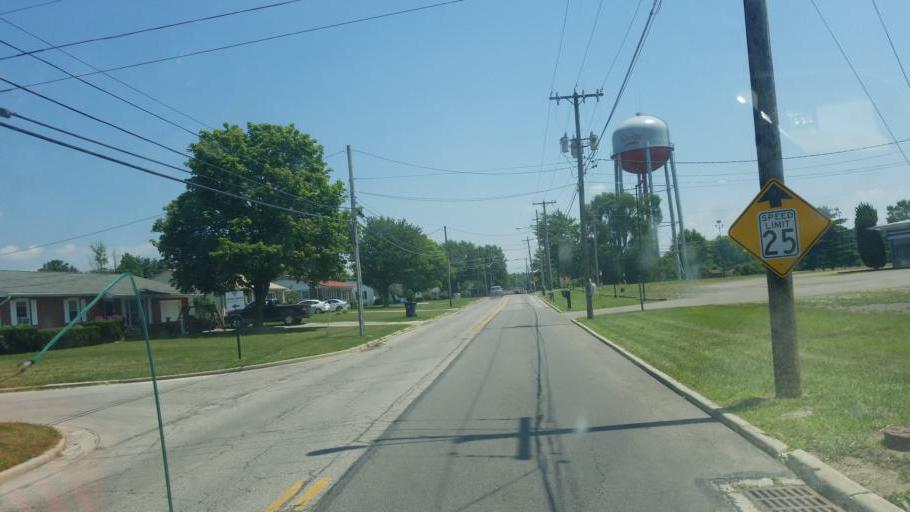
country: US
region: Ohio
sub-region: Richland County
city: Shelby
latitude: 40.8688
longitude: -82.6519
